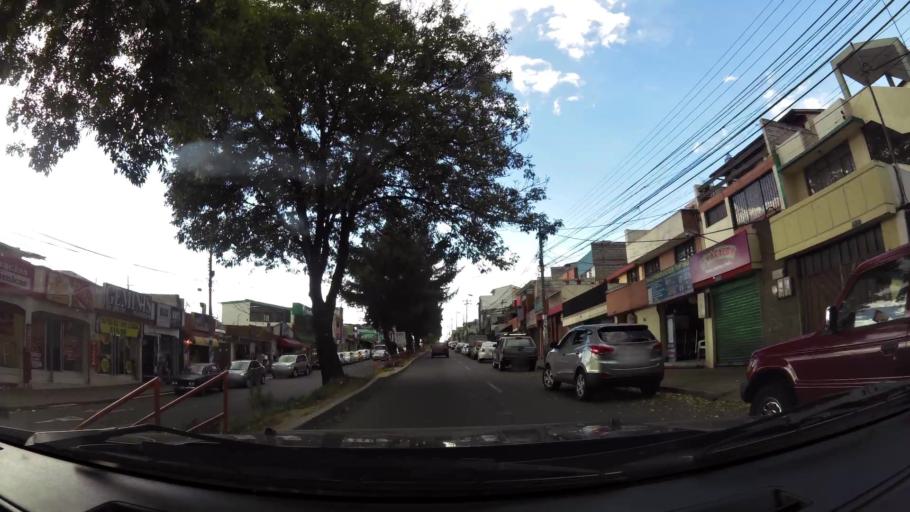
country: EC
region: Pichincha
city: Quito
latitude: -0.1278
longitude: -78.4872
